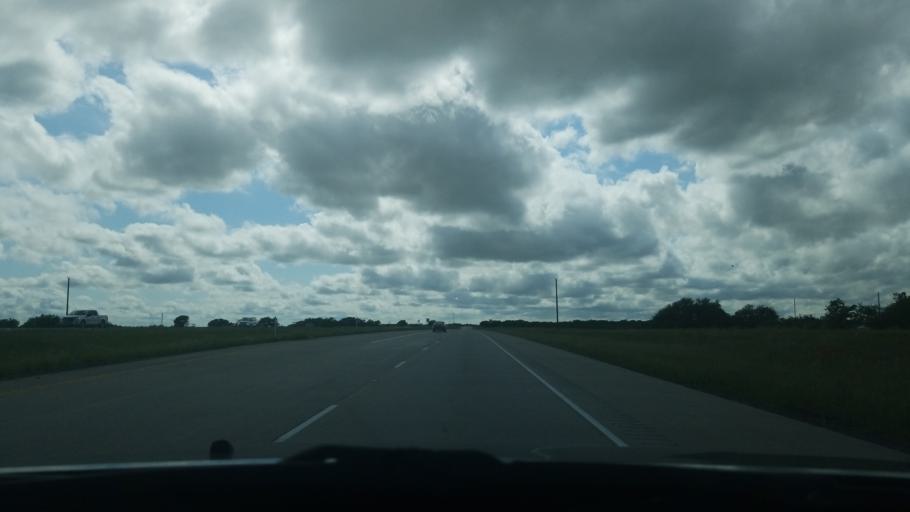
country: US
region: Texas
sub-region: Wise County
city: Decatur
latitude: 33.2453
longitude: -97.4885
